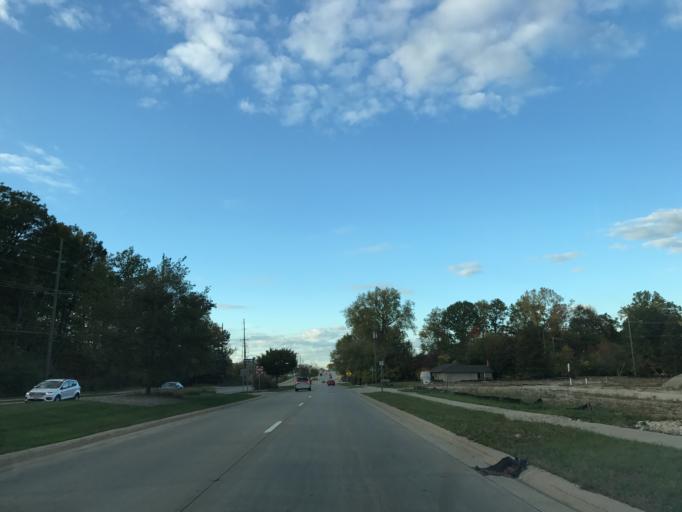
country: US
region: Michigan
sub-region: Oakland County
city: Farmington Hills
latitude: 42.4898
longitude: -83.3580
